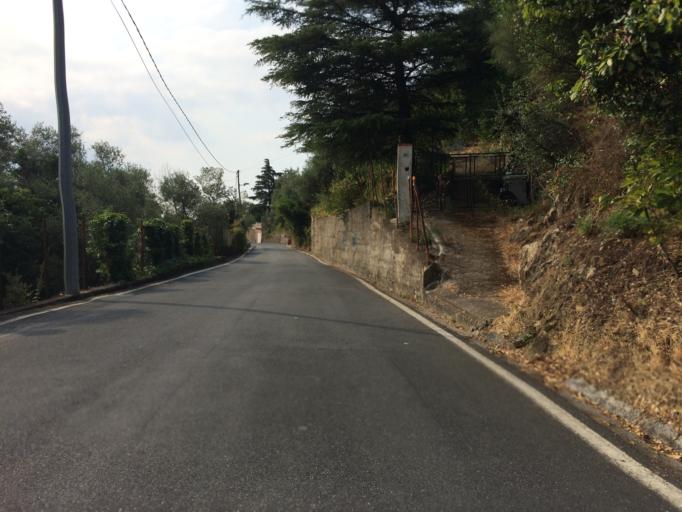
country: IT
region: Liguria
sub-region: Provincia di Imperia
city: San Remo
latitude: 43.8370
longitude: 7.7568
